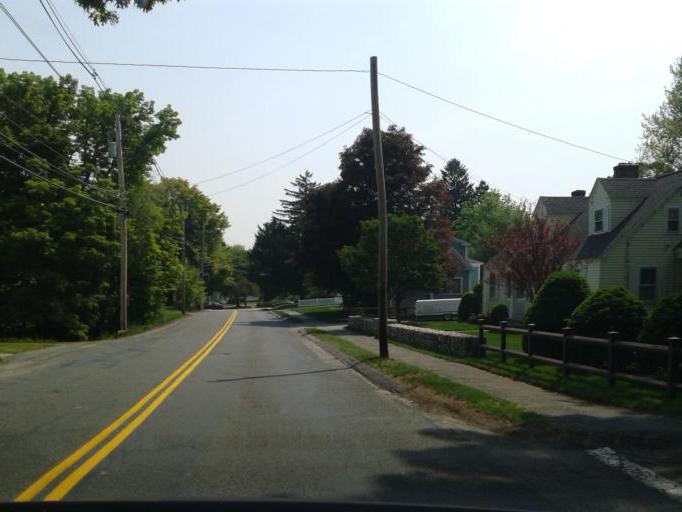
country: US
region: Massachusetts
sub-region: Worcester County
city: Westborough
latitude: 42.2711
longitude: -71.6231
